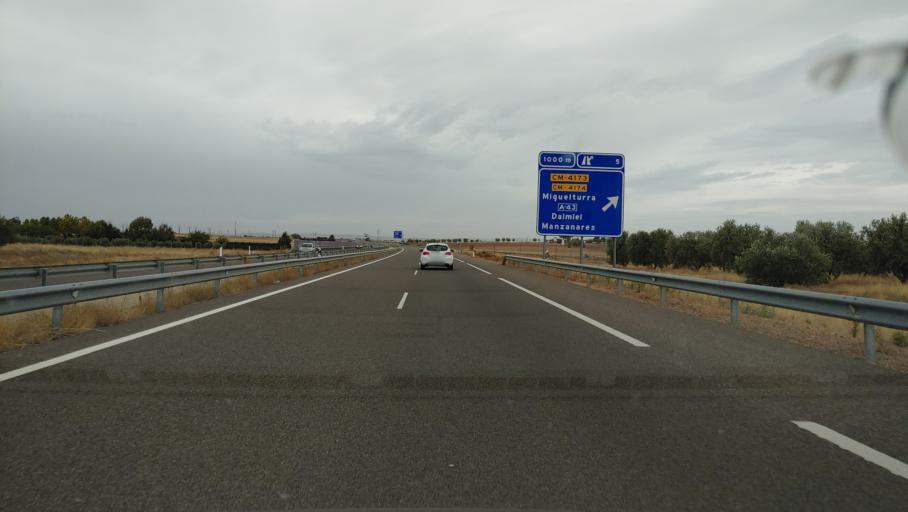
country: ES
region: Castille-La Mancha
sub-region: Provincia de Ciudad Real
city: Miguelturra
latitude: 38.9358
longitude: -3.8645
